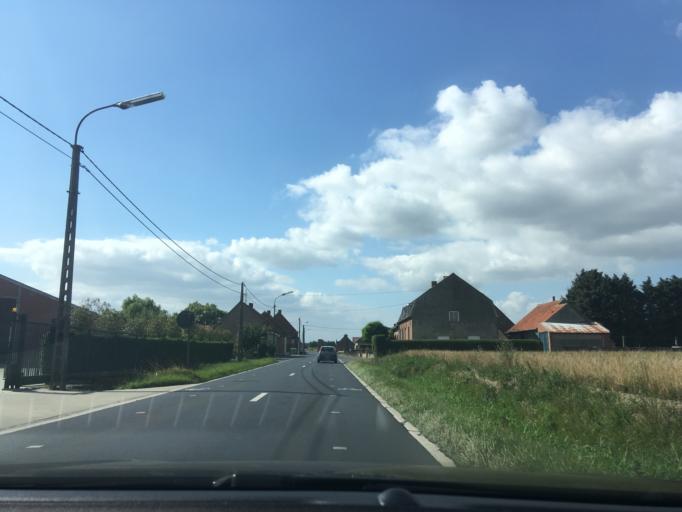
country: BE
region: Flanders
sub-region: Provincie West-Vlaanderen
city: Moorslede
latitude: 50.9218
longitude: 3.0406
